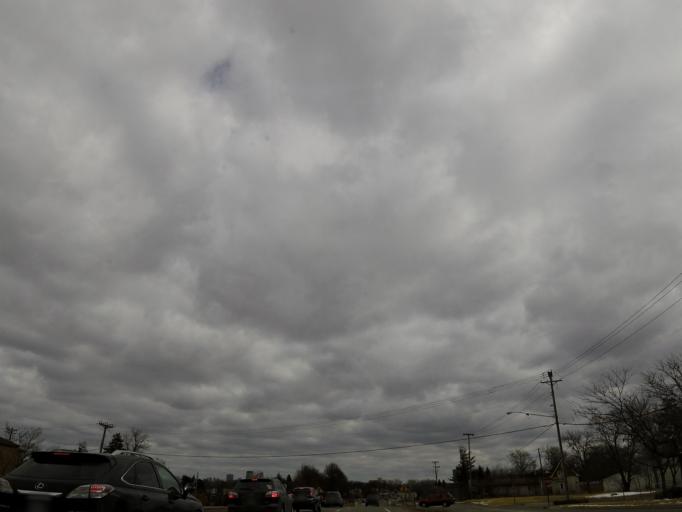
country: US
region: Minnesota
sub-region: Hennepin County
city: Saint Louis Park
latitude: 44.9469
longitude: -93.3349
